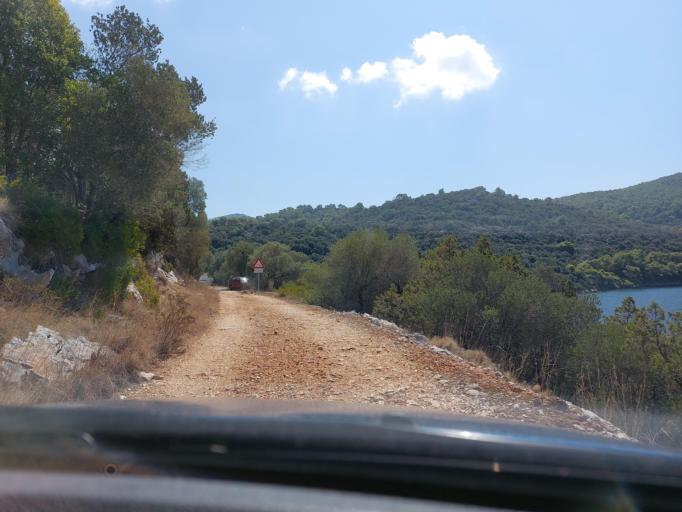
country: HR
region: Dubrovacko-Neretvanska
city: Smokvica
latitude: 42.7737
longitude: 16.8375
